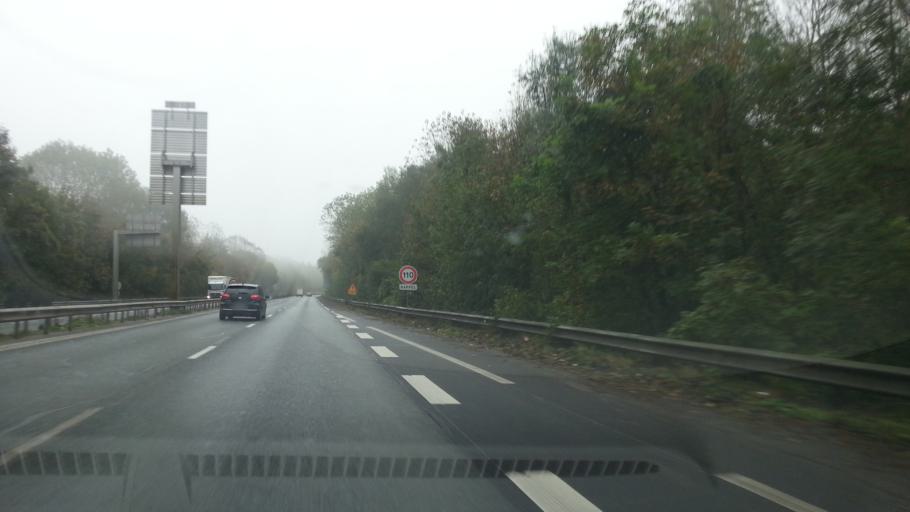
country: FR
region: Picardie
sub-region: Departement de l'Oise
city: Fitz-James
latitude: 49.3887
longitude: 2.4158
